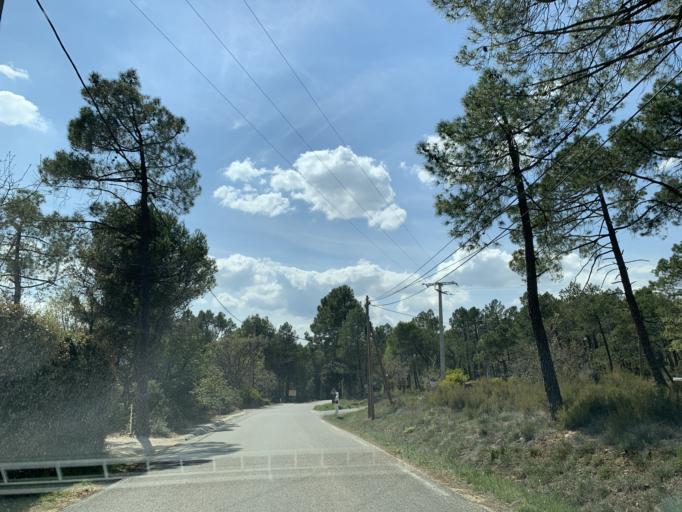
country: FR
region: Provence-Alpes-Cote d'Azur
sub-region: Departement du Vaucluse
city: Roussillon
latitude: 43.8936
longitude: 5.2822
